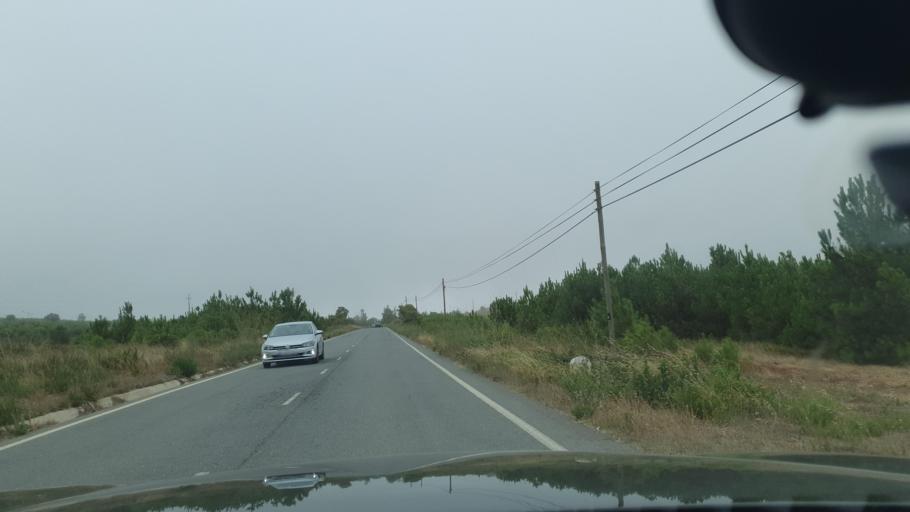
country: PT
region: Beja
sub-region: Odemira
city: Sao Teotonio
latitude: 37.5254
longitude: -8.7138
